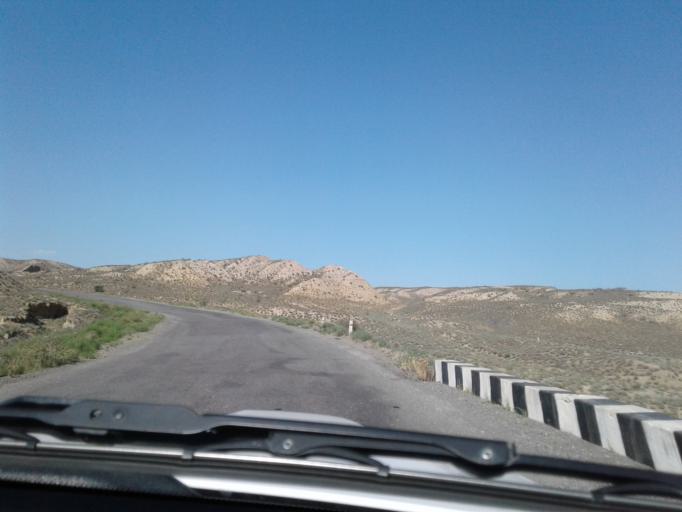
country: TM
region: Balkan
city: Magtymguly
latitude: 38.6507
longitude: 56.2753
